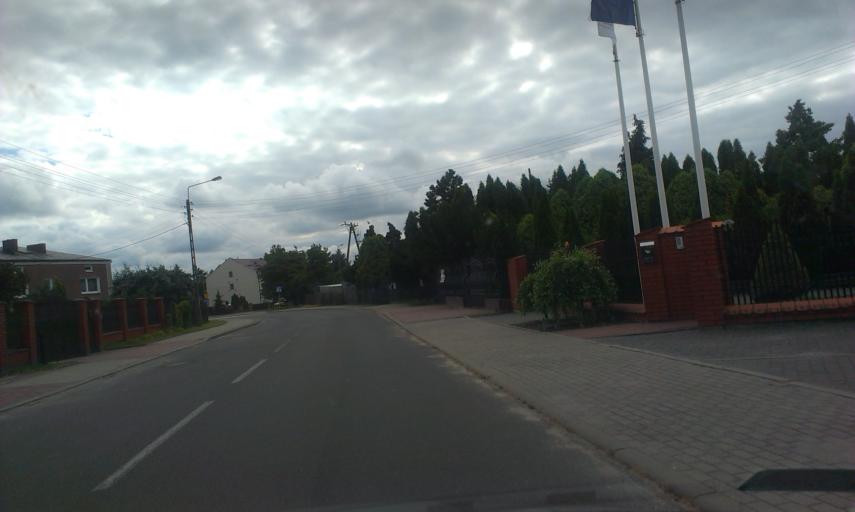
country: PL
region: Masovian Voivodeship
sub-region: Powiat zyrardowski
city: Mszczonow
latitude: 51.9749
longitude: 20.5284
